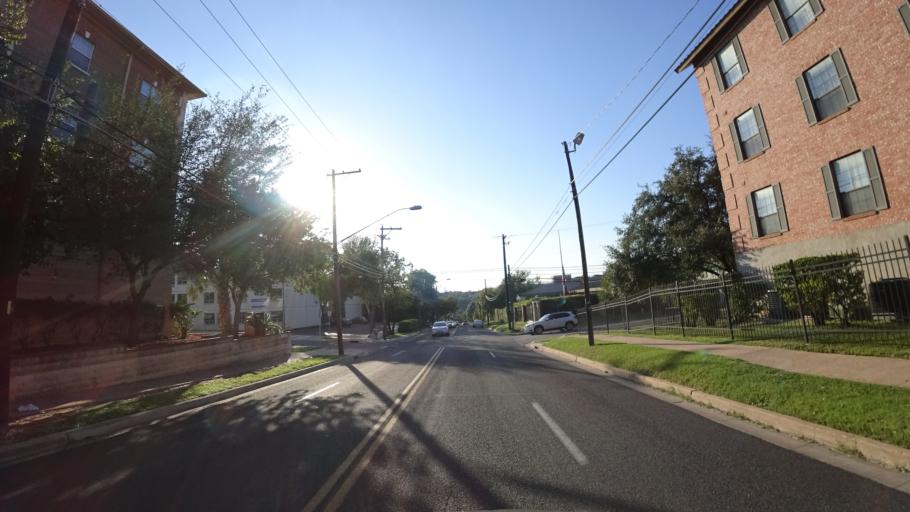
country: US
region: Texas
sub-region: Travis County
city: Austin
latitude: 30.2882
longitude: -97.7489
